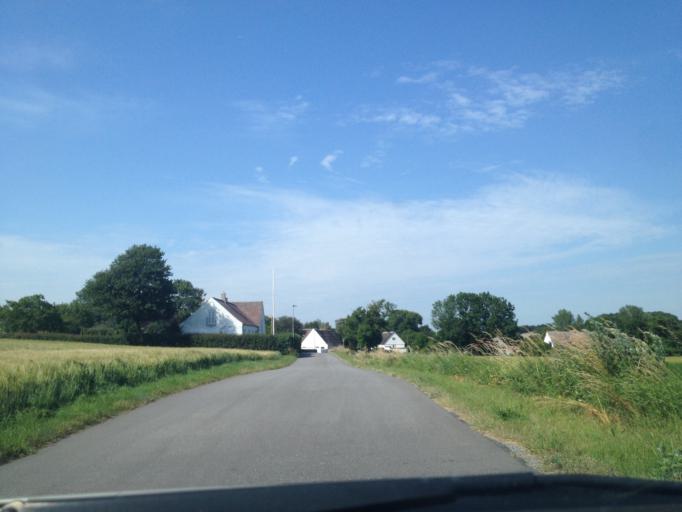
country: DK
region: Central Jutland
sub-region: Samso Kommune
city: Tranebjerg
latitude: 55.8366
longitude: 10.5549
